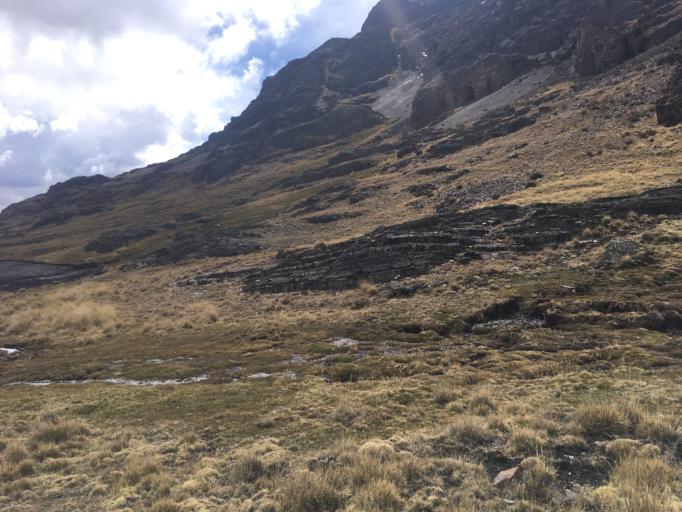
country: BO
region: La Paz
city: La Paz
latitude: -16.3926
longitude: -67.9644
